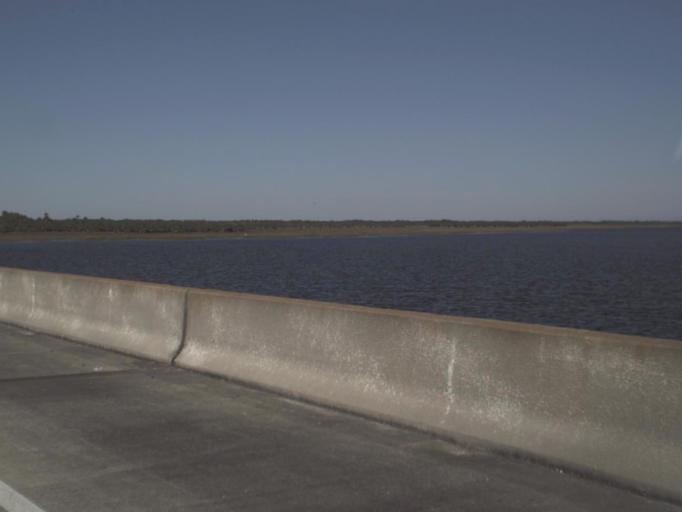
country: US
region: Florida
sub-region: Seminole County
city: Oviedo
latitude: 28.7168
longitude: -81.2416
